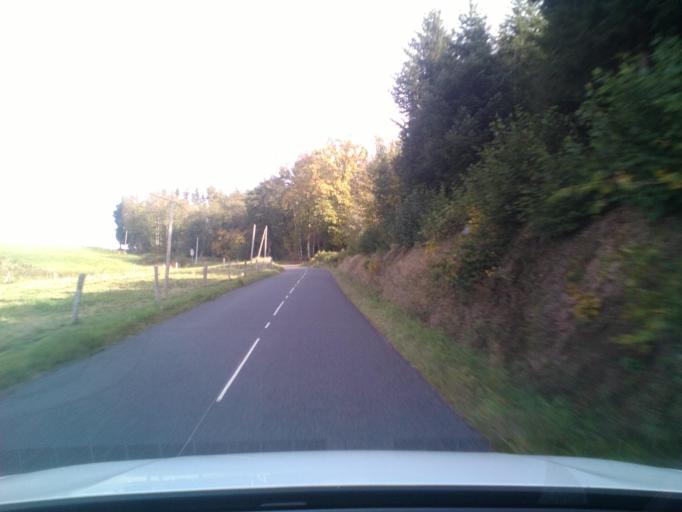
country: FR
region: Lorraine
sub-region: Departement des Vosges
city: Senones
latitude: 48.3687
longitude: 7.0305
